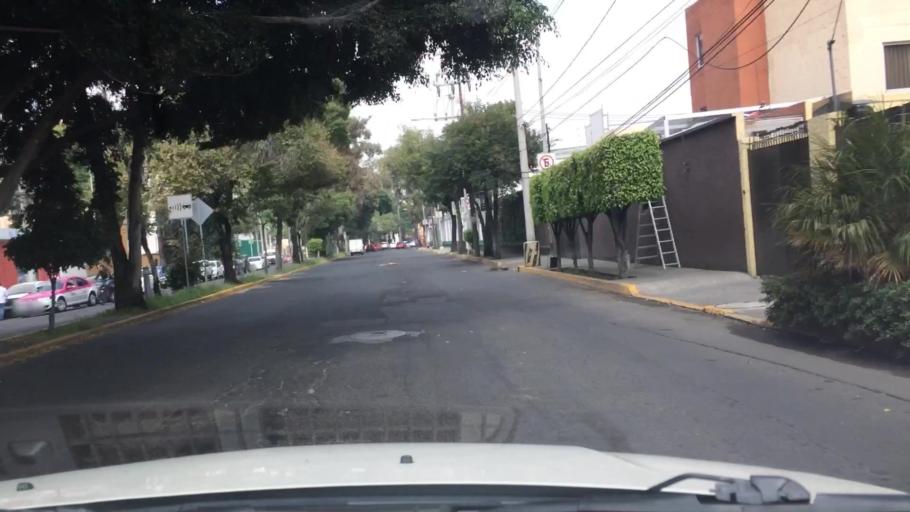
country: MX
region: Mexico City
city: Coyoacan
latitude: 19.3357
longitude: -99.1483
